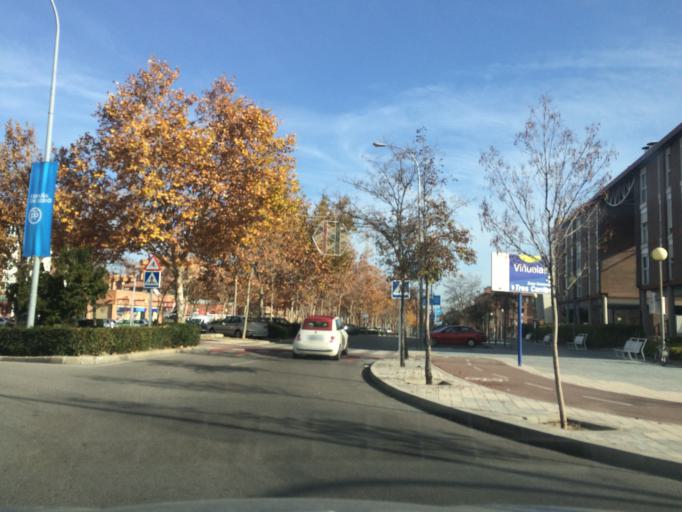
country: ES
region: Madrid
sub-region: Provincia de Madrid
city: Tres Cantos
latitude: 40.5954
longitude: -3.7066
